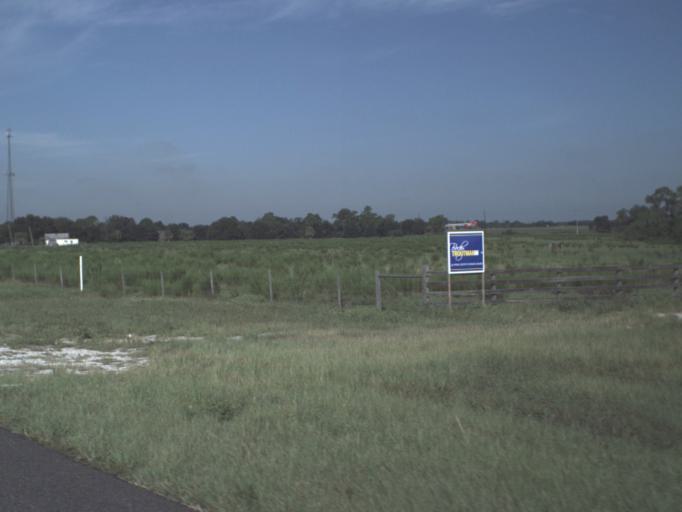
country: US
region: Florida
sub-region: Polk County
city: Wahneta
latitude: 27.9099
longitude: -81.7540
